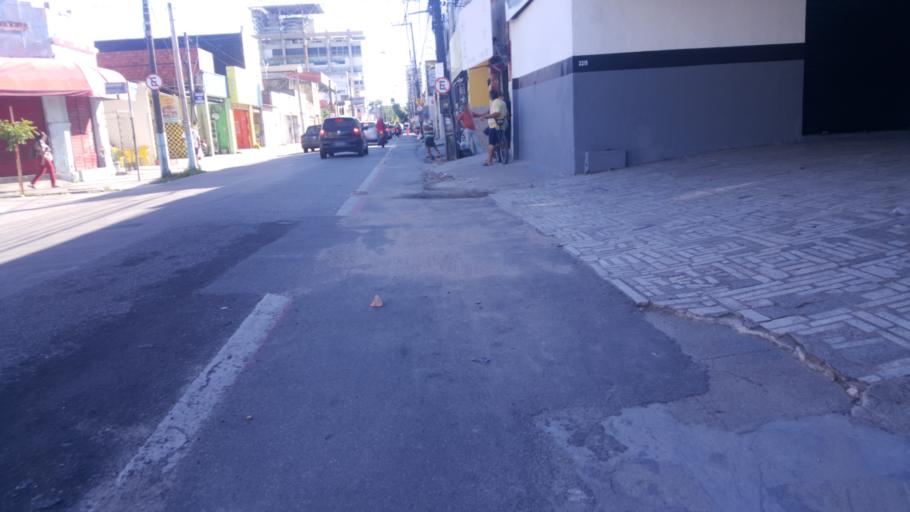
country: BR
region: Ceara
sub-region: Fortaleza
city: Fortaleza
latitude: -3.7378
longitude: -38.5318
